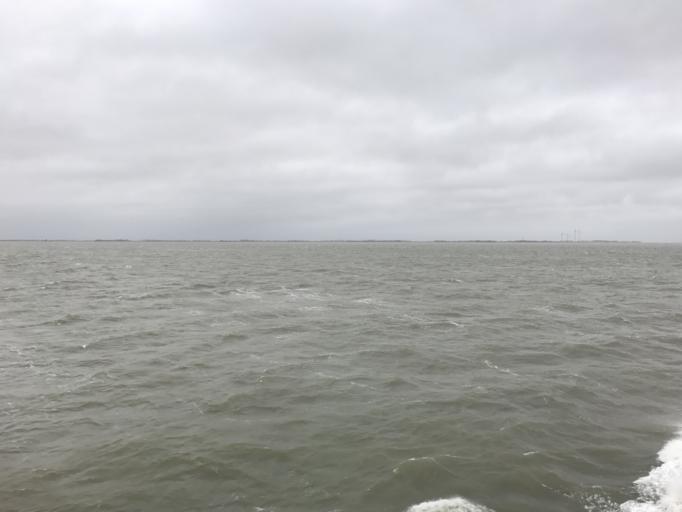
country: NL
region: Groningen
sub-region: Gemeente Delfzijl
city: Delfzijl
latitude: 53.4010
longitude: 6.9491
